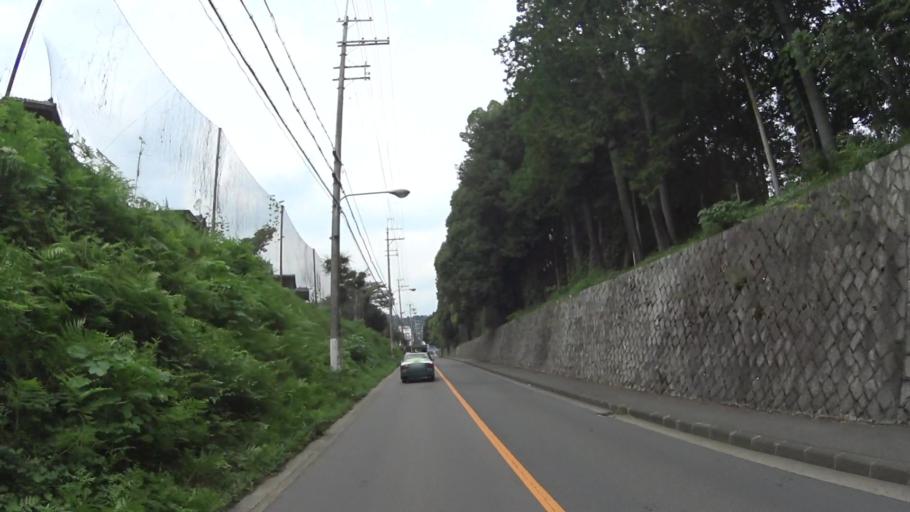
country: JP
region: Kyoto
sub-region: Kyoto-shi
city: Kamigyo-ku
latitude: 35.0657
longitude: 135.7510
